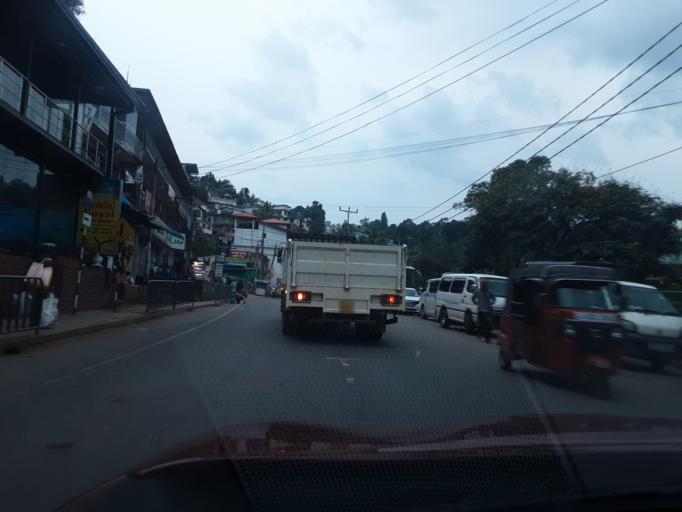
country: LK
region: Central
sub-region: Nuwara Eliya District
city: Nuwara Eliya
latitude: 6.9049
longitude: 80.9095
